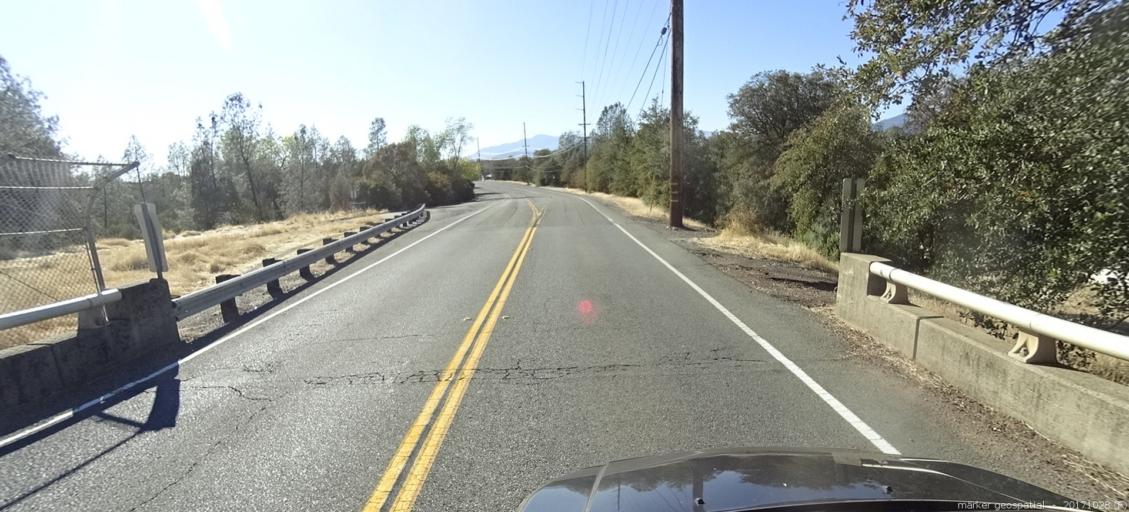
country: US
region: California
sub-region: Shasta County
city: Redding
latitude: 40.6311
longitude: -122.3977
